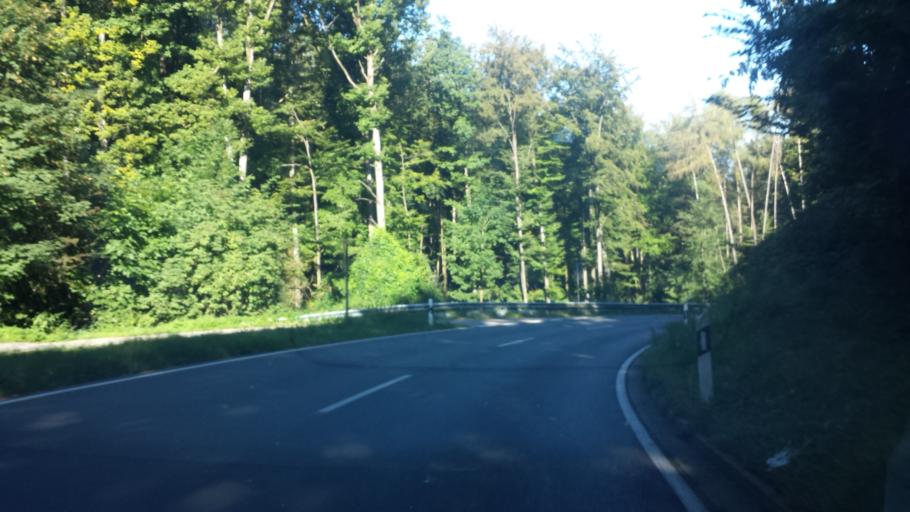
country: DE
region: Bavaria
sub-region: Lower Bavaria
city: Ihrlerstein
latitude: 48.9072
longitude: 11.8584
